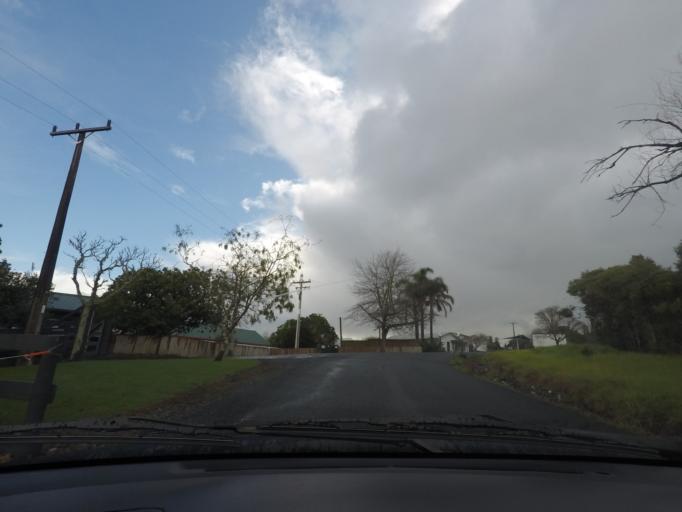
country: NZ
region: Auckland
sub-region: Auckland
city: Warkworth
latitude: -36.4295
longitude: 174.7314
